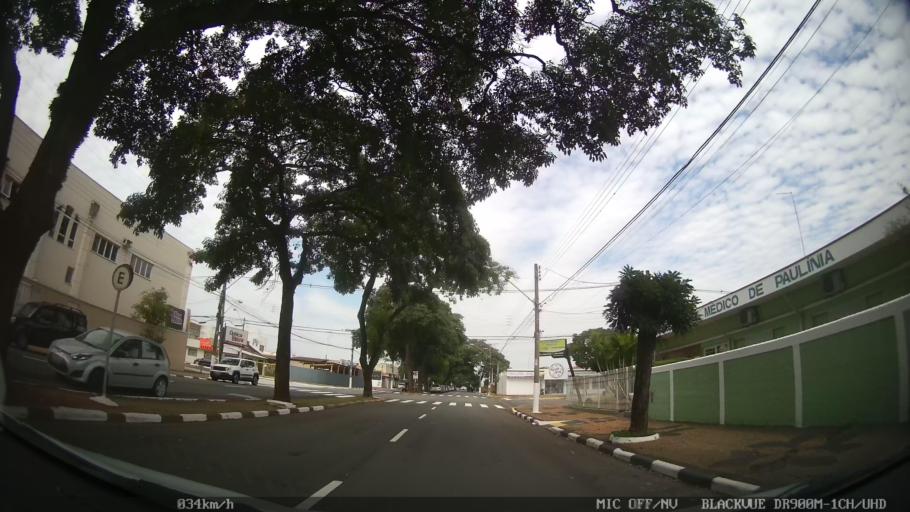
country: BR
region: Sao Paulo
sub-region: Paulinia
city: Paulinia
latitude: -22.7672
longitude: -47.1503
